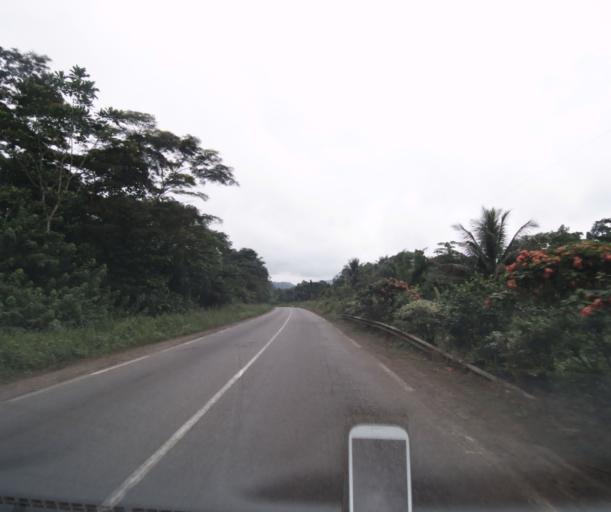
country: CM
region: Littoral
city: Edea
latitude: 3.8065
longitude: 10.2591
